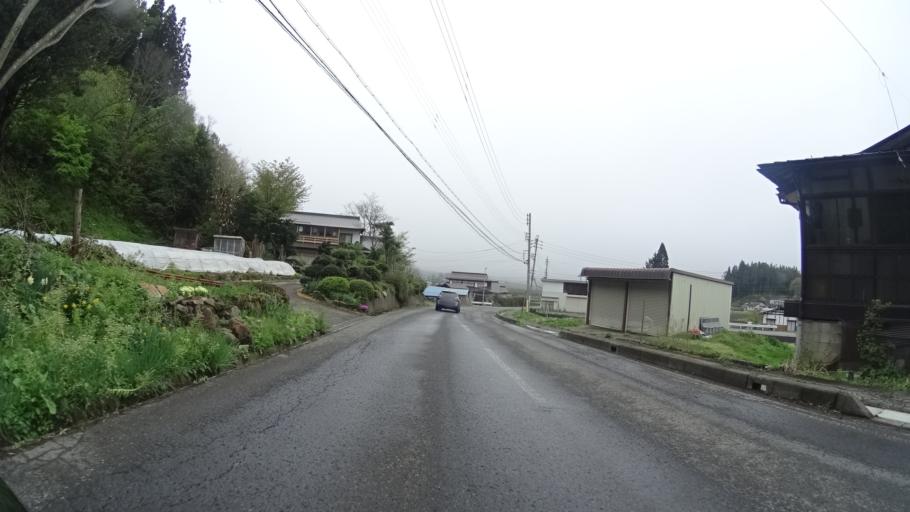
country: JP
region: Nagano
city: Nagano-shi
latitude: 36.7675
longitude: 138.1992
